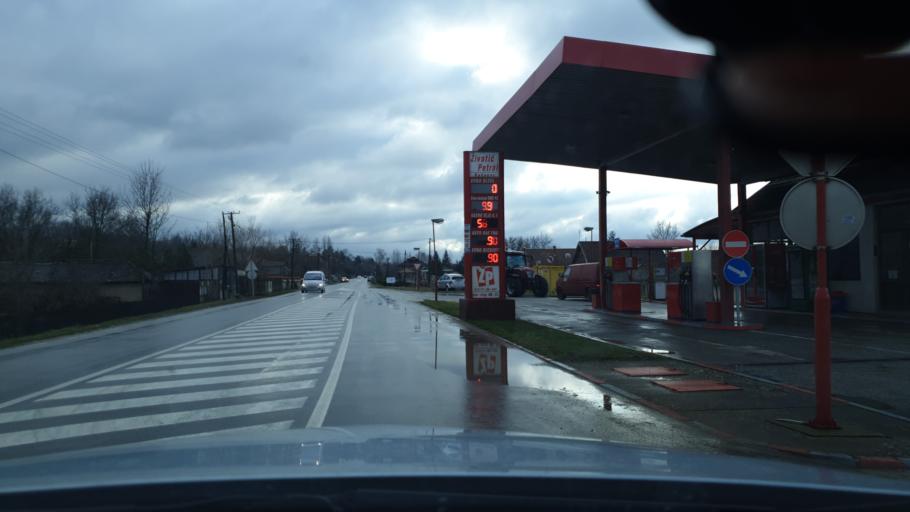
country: RS
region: Central Serbia
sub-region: Branicevski Okrug
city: Malo Crnice
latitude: 44.4598
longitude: 21.3380
